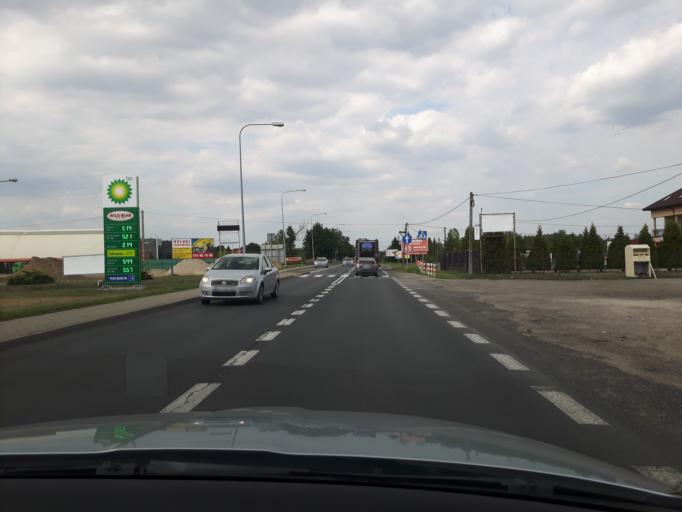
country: PL
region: Masovian Voivodeship
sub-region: Powiat legionowski
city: Stanislawow Pierwszy
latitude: 52.3365
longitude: 21.0294
